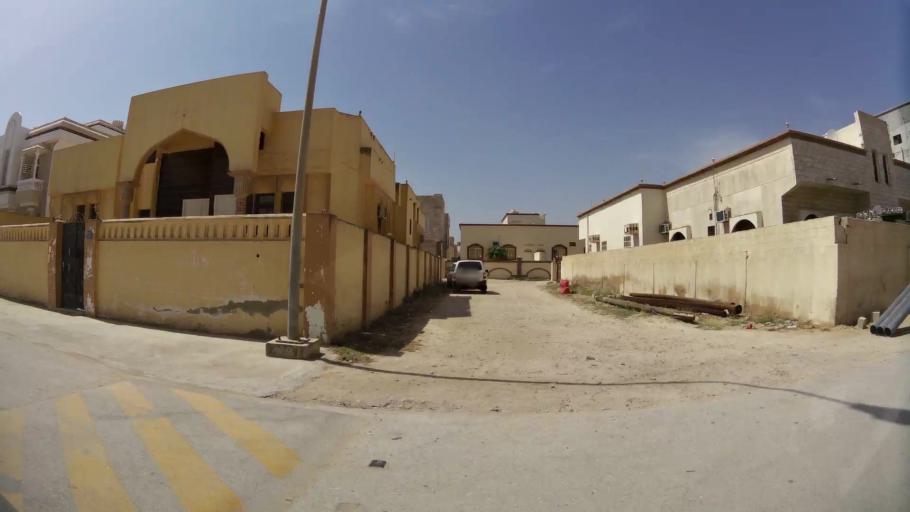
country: OM
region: Zufar
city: Salalah
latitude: 17.0426
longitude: 54.1500
